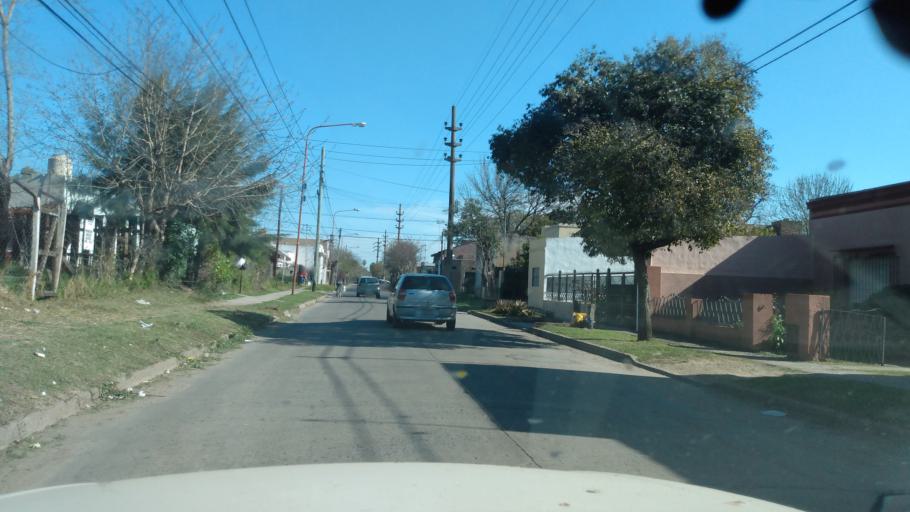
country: AR
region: Buenos Aires
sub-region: Partido de Lujan
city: Lujan
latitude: -34.5739
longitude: -59.1000
